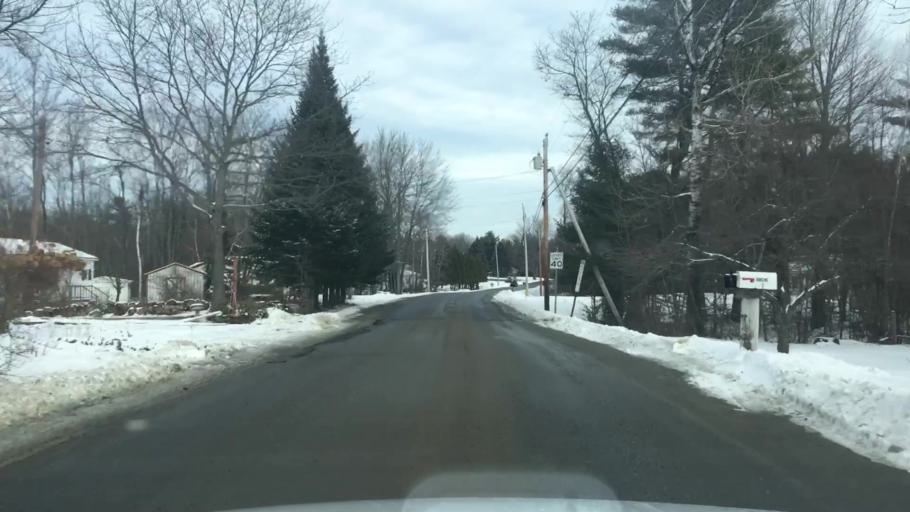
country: US
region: Maine
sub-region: Kennebec County
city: Chelsea
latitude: 44.2776
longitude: -69.6743
